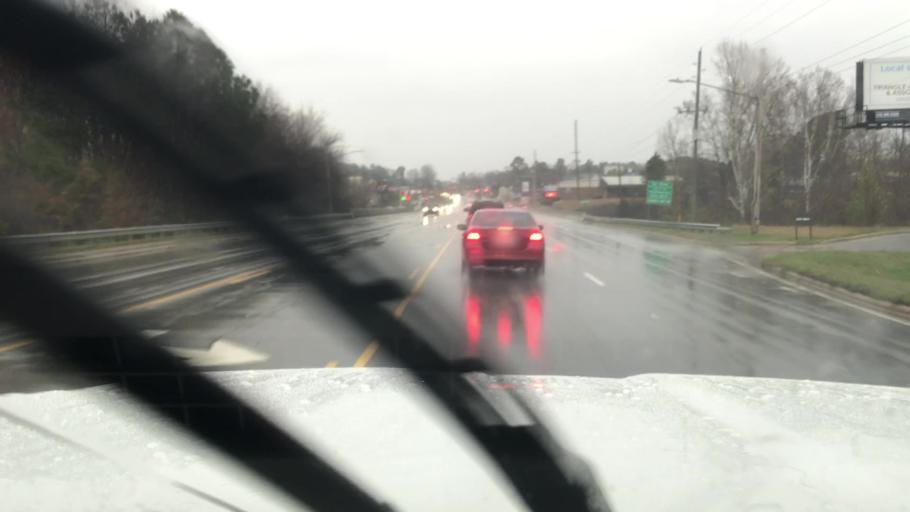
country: US
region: North Carolina
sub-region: Franklin County
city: Louisburg
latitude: 36.0934
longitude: -78.2983
